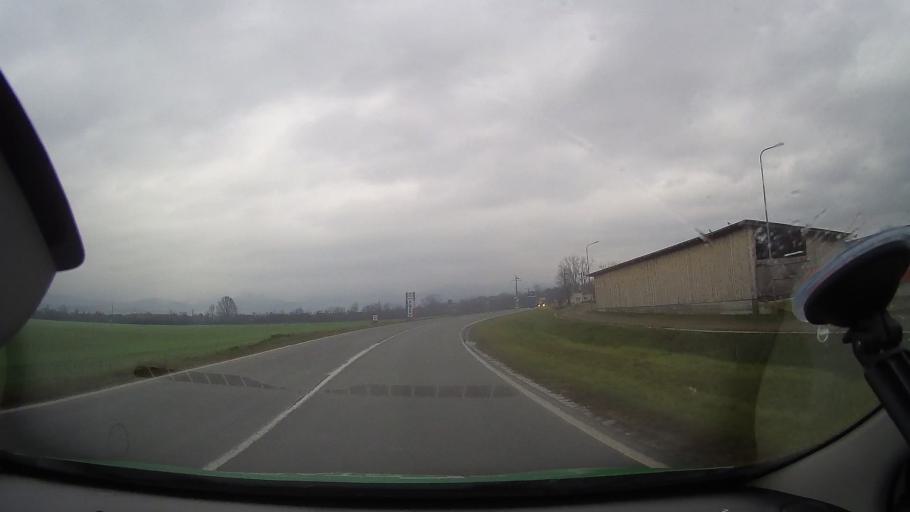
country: RO
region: Arad
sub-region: Comuna Gurahont
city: Gurahont
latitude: 46.2763
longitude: 22.2962
